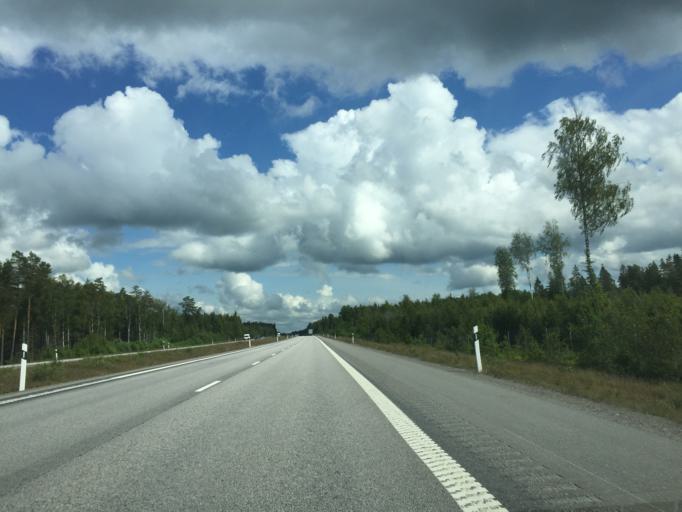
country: SE
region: OErebro
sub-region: Lindesbergs Kommun
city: Fellingsbro
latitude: 59.3490
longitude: 15.5552
